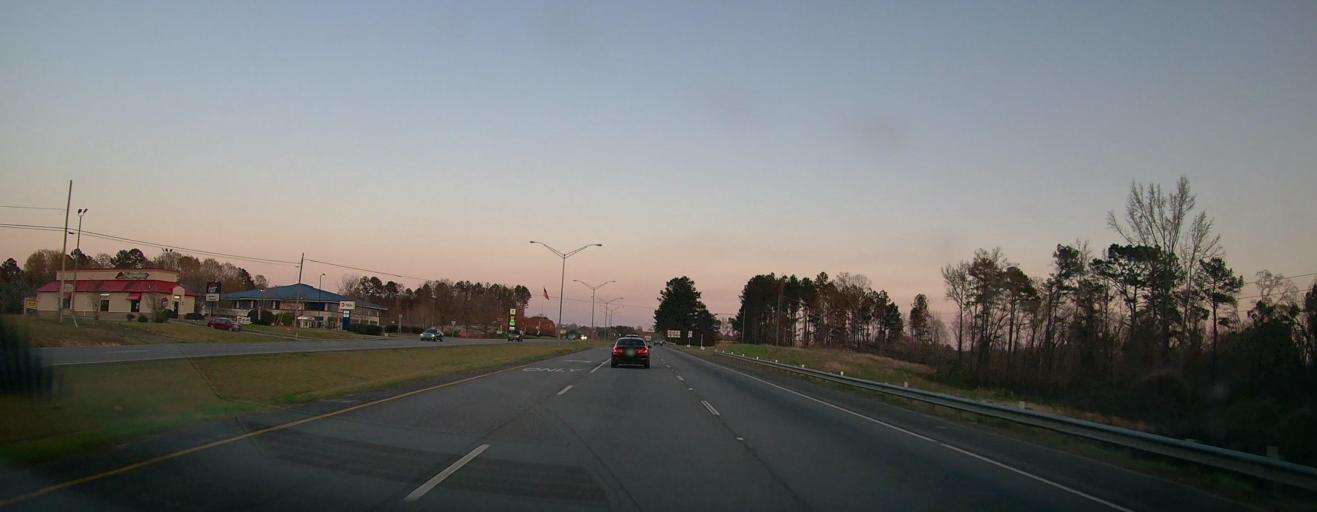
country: US
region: Alabama
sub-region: Tallapoosa County
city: Alexander City
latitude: 32.9185
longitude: -85.9556
